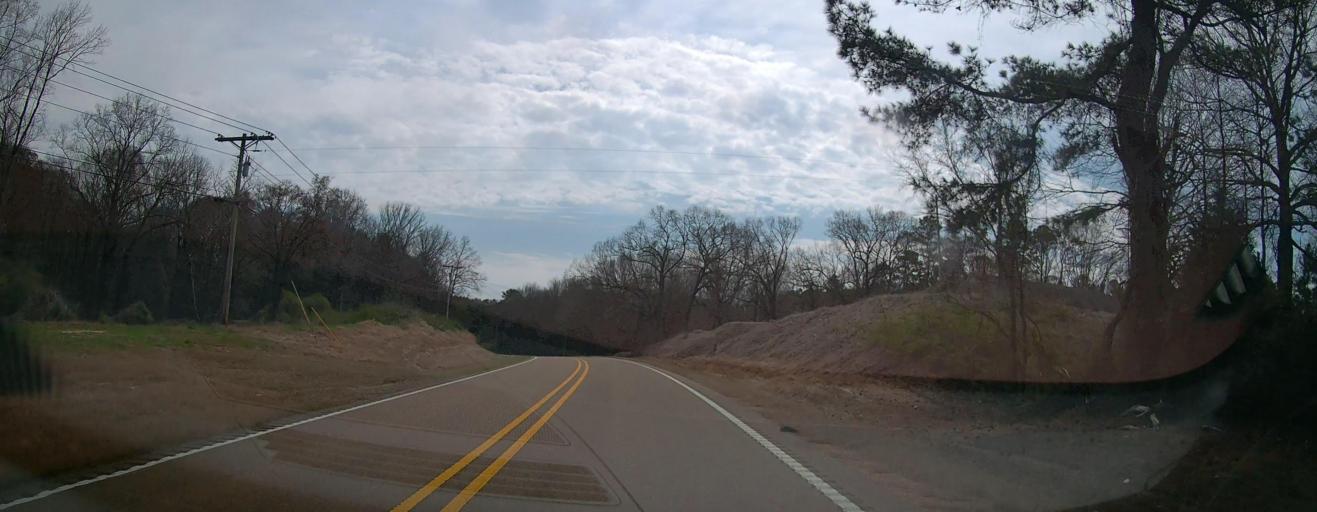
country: US
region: Mississippi
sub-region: Marshall County
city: Holly Springs
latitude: 34.7209
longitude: -89.4142
